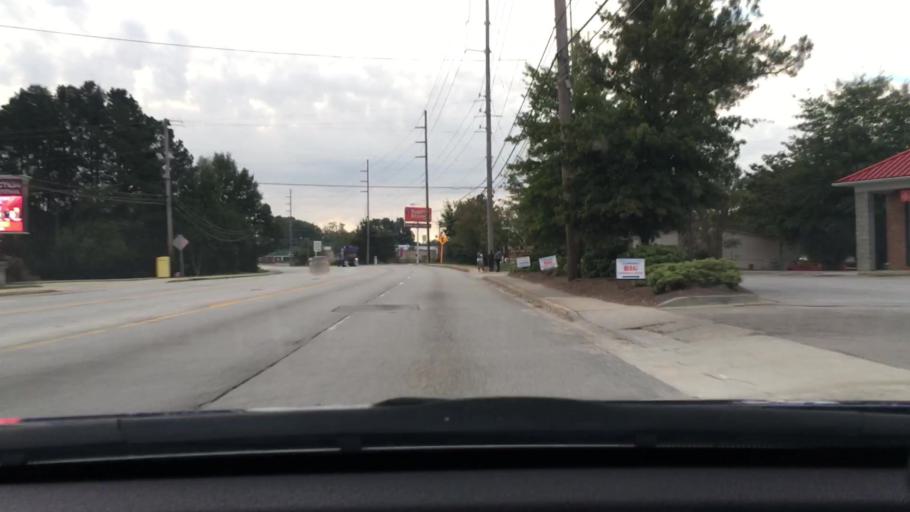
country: US
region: South Carolina
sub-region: Lexington County
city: Saint Andrews
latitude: 34.0552
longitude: -81.1103
